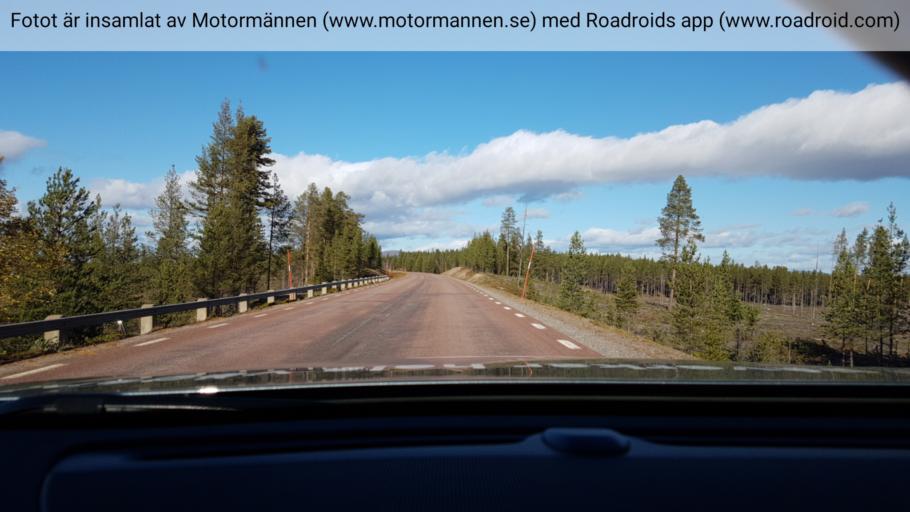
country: SE
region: Norrbotten
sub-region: Arjeplogs Kommun
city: Arjeplog
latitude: 66.0303
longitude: 18.0602
